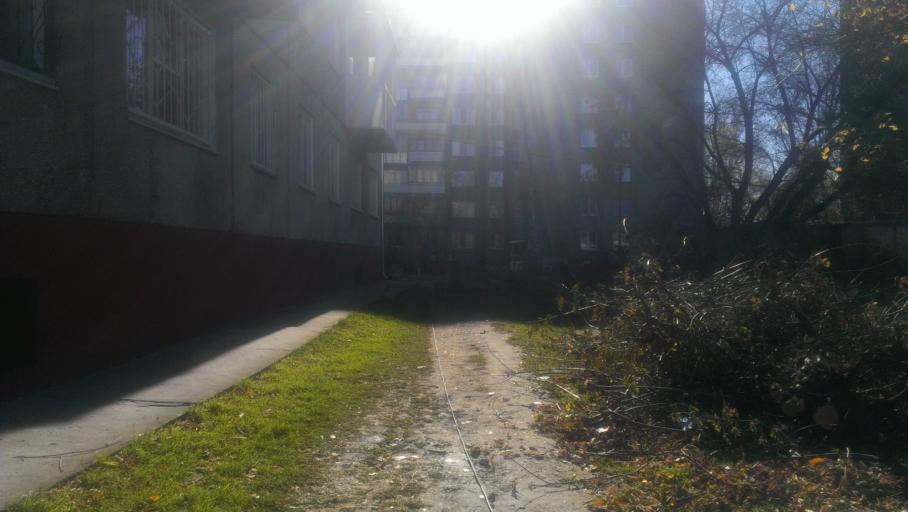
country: RU
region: Altai Krai
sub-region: Gorod Barnaulskiy
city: Barnaul
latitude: 53.3622
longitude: 83.6851
